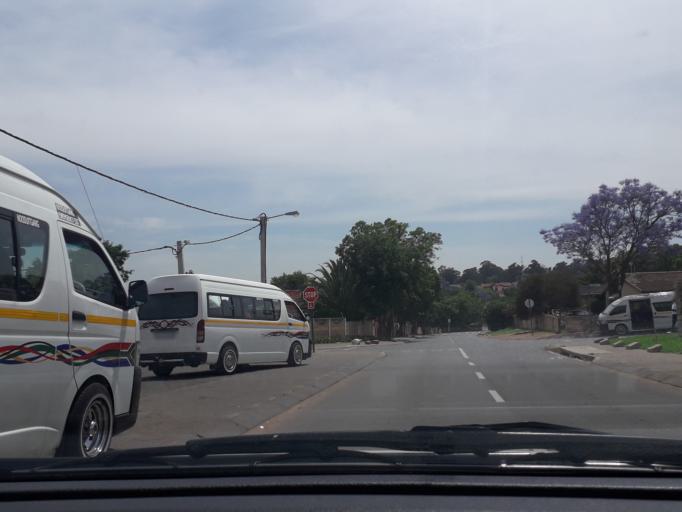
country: ZA
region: Gauteng
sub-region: City of Johannesburg Metropolitan Municipality
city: Roodepoort
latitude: -26.2044
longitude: 27.9120
